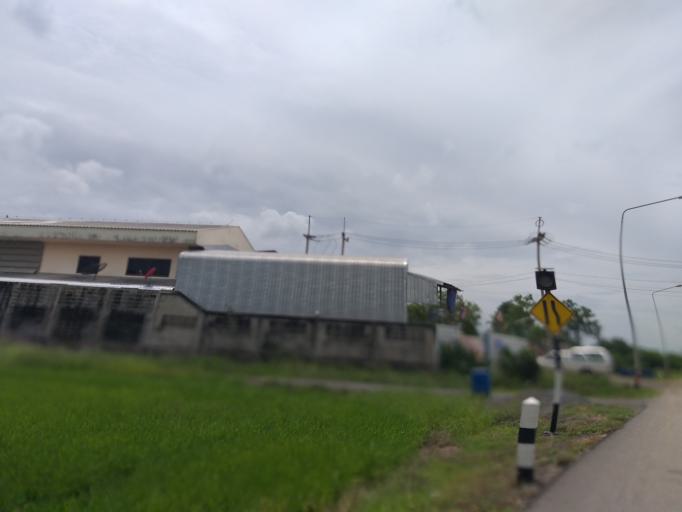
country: TH
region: Pathum Thani
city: Nong Suea
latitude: 14.0522
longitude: 100.8709
